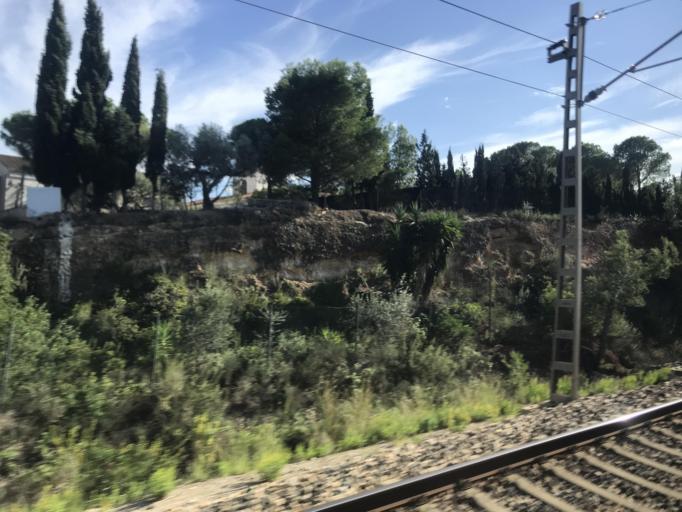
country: ES
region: Catalonia
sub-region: Provincia de Tarragona
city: L'Ampolla
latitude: 40.8290
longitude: 0.7362
